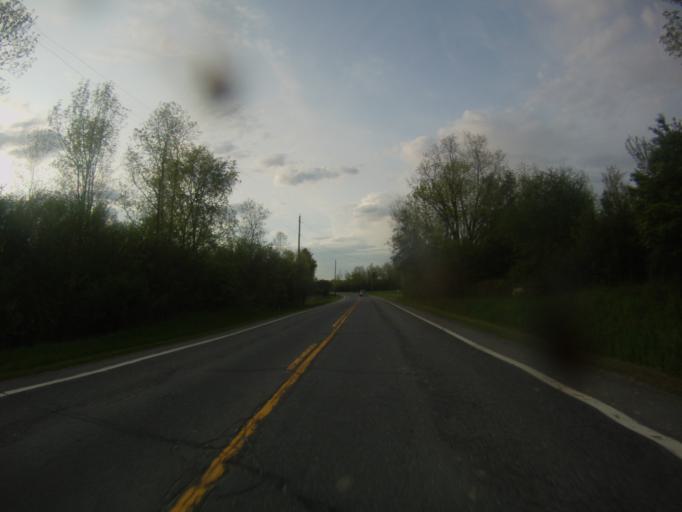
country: US
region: New York
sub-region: Essex County
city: Port Henry
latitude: 44.0094
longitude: -73.4195
